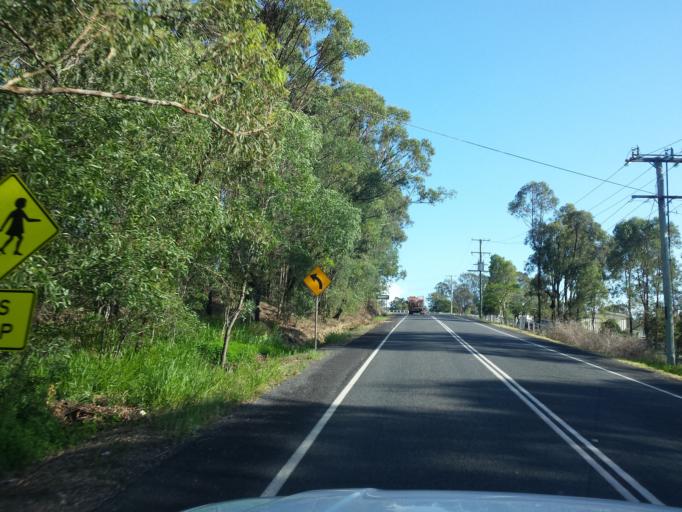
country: AU
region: Queensland
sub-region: Logan
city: Windaroo
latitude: -27.7692
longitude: 153.1911
